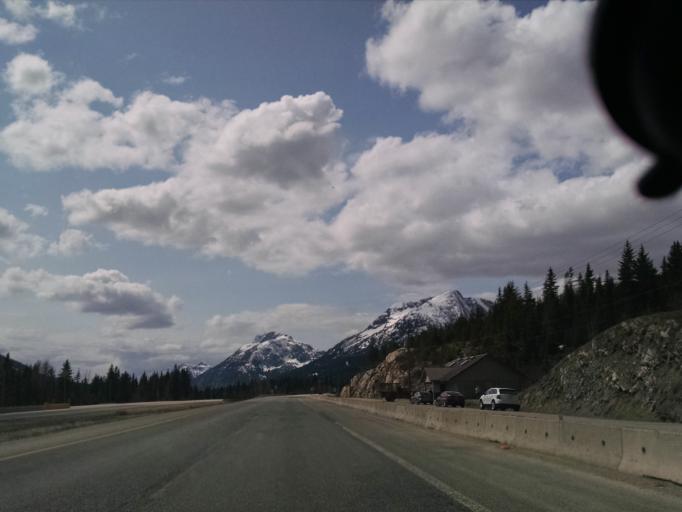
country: CA
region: British Columbia
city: Hope
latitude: 49.6311
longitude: -121.0156
